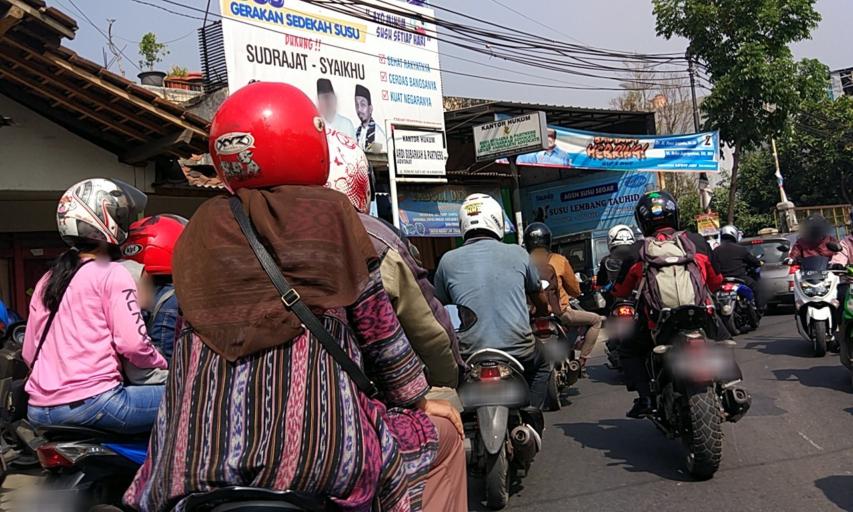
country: ID
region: West Java
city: Cimahi
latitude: -6.8940
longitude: 107.5616
